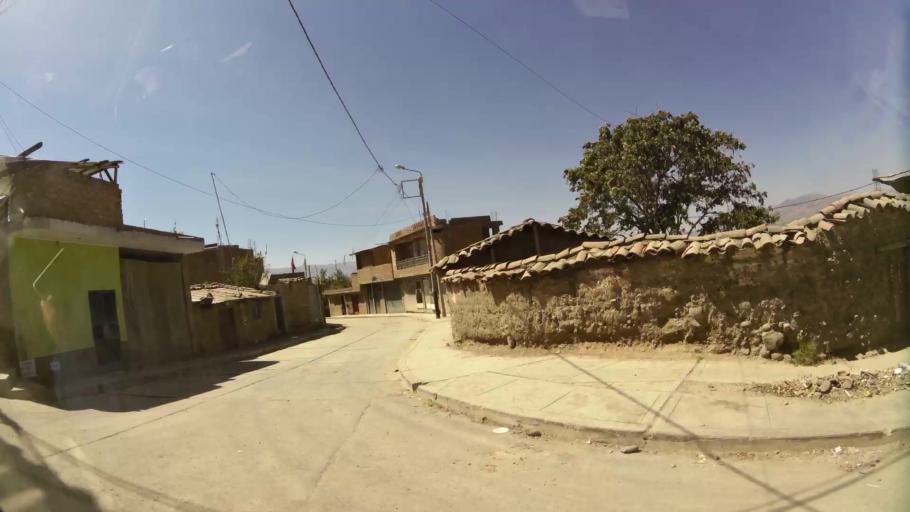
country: PE
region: Ayacucho
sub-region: Provincia de Huamanga
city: Ayacucho
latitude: -13.1612
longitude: -74.2374
